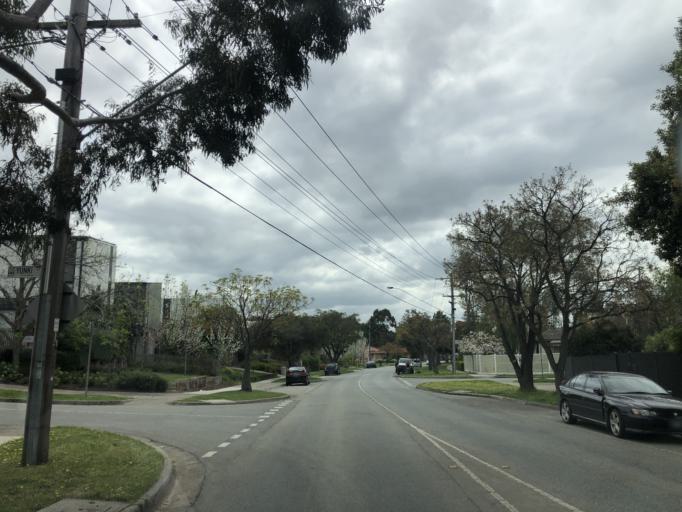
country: AU
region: Victoria
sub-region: Monash
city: Ashwood
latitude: -37.8716
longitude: 145.1001
